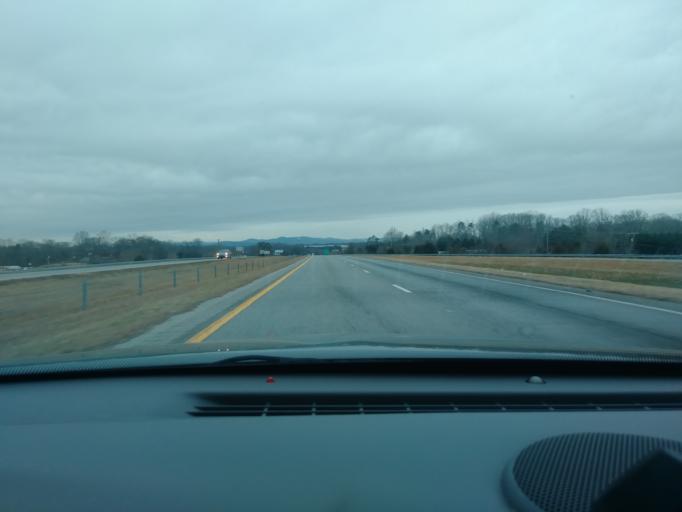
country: US
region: North Carolina
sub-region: Yadkin County
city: Jonesville
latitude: 36.1193
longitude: -80.7952
